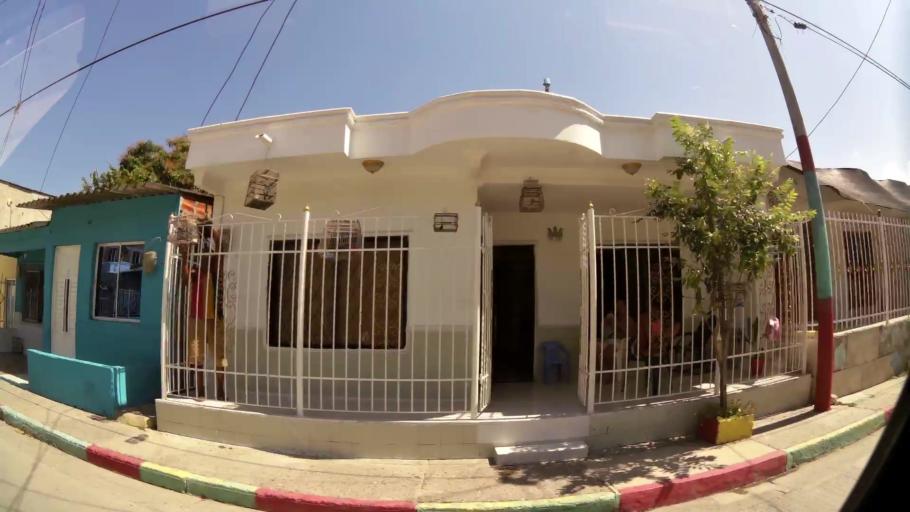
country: CO
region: Bolivar
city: Cartagena
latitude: 10.3851
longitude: -75.5033
